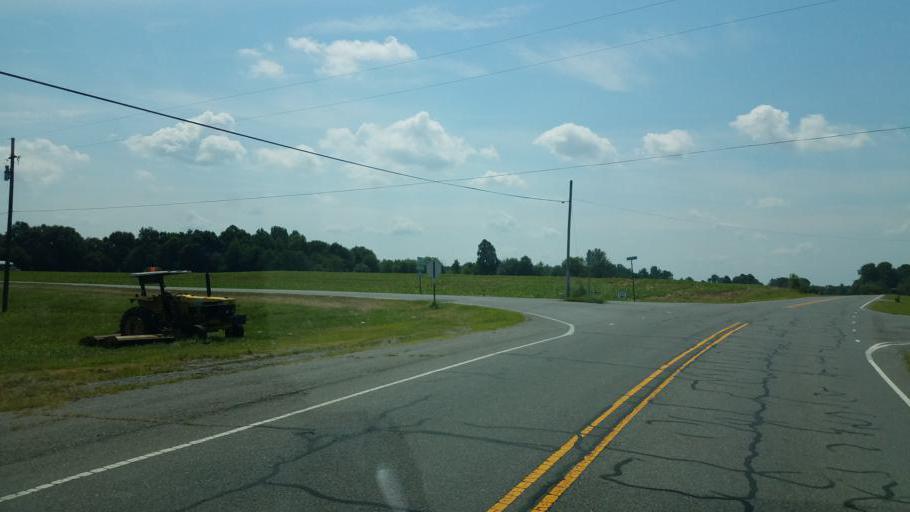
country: US
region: North Carolina
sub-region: Gaston County
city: Cherryville
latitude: 35.4638
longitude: -81.4356
